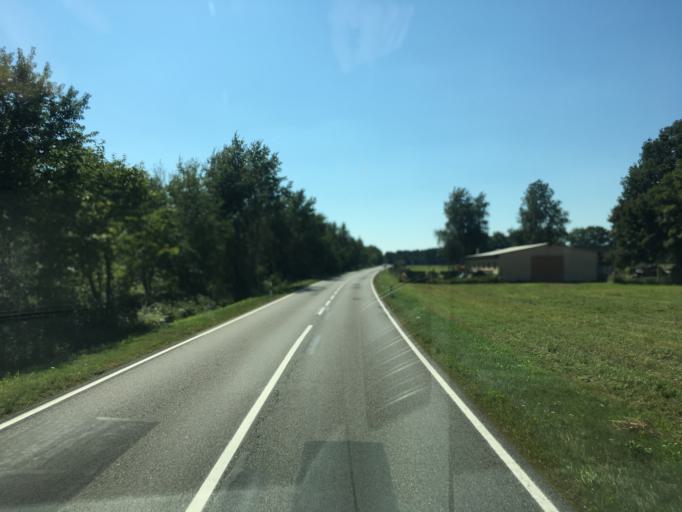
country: DE
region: Brandenburg
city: Welzow
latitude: 51.5226
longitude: 14.1793
